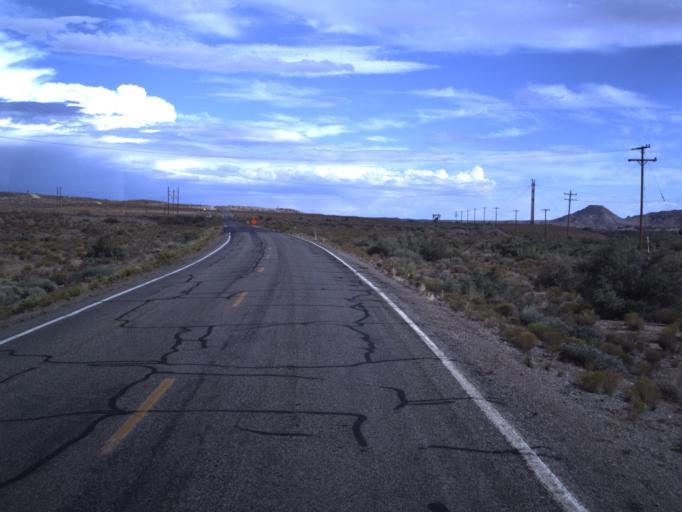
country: US
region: Utah
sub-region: San Juan County
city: Blanding
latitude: 37.2439
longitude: -109.2510
